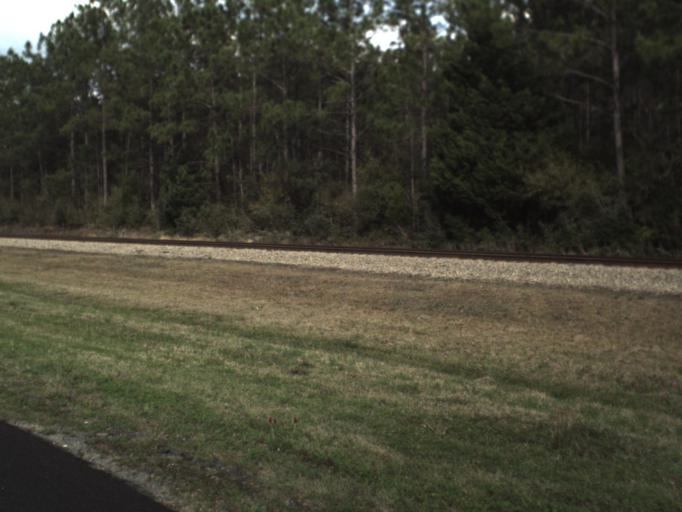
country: US
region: Florida
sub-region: Bay County
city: Youngstown
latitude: 30.3430
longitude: -85.4410
